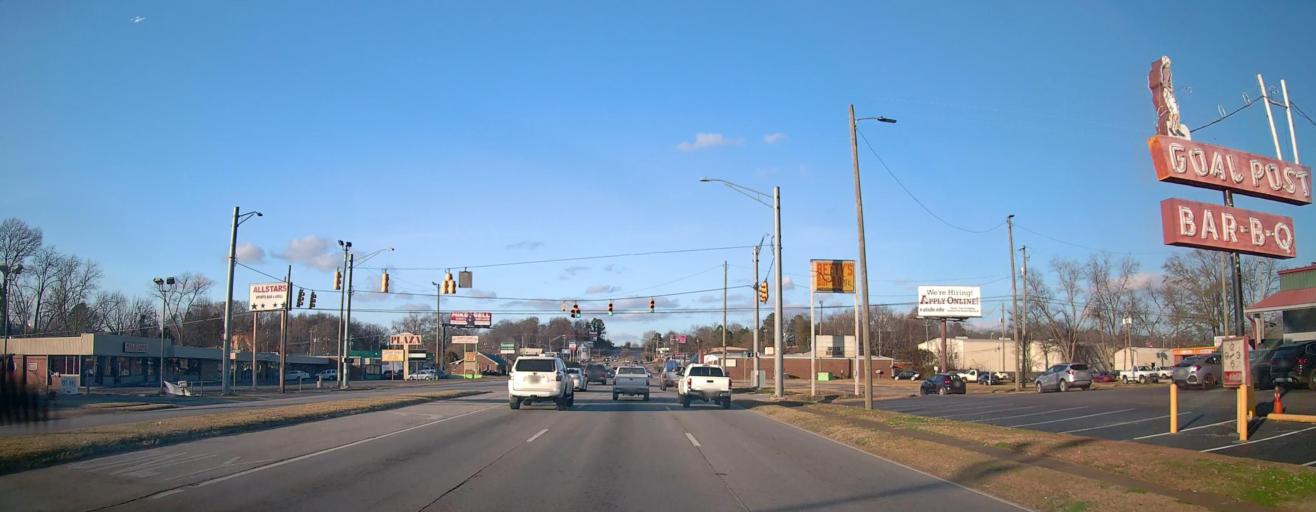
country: US
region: Alabama
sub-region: Calhoun County
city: Anniston
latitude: 33.6417
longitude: -85.8258
